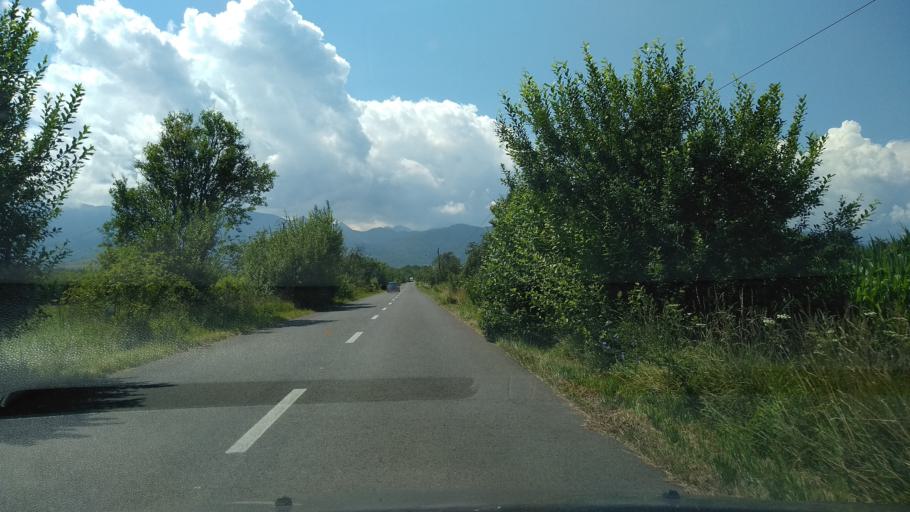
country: RO
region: Hunedoara
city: Salasu de Sus
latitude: 45.5207
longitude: 22.9615
